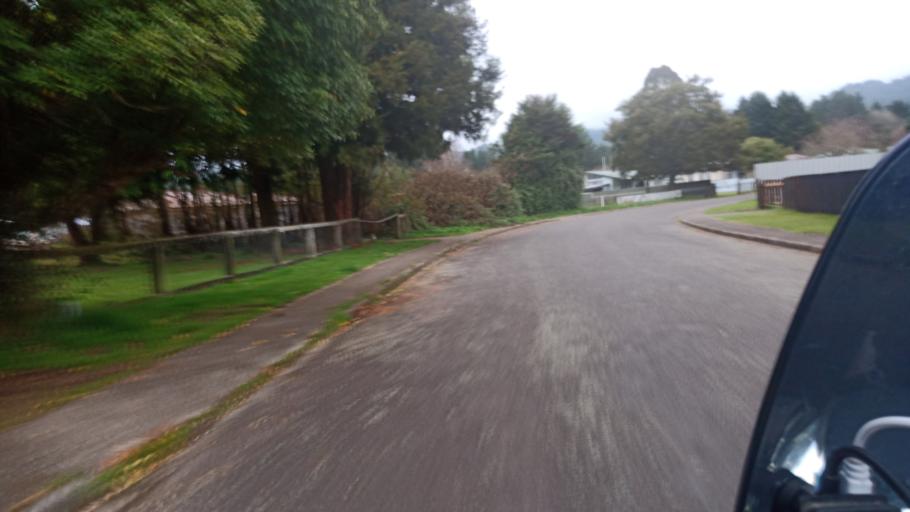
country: NZ
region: Bay of Plenty
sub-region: Whakatane District
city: Murupara
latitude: -38.6437
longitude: 176.7313
